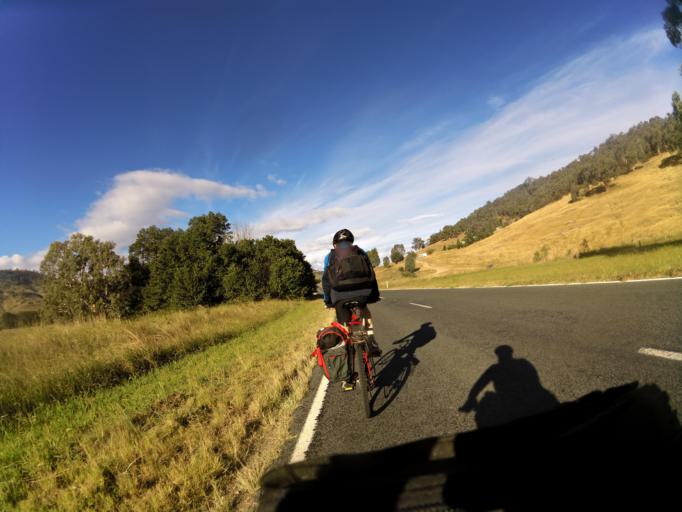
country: AU
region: New South Wales
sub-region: Greater Hume Shire
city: Holbrook
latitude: -35.9727
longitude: 147.7995
